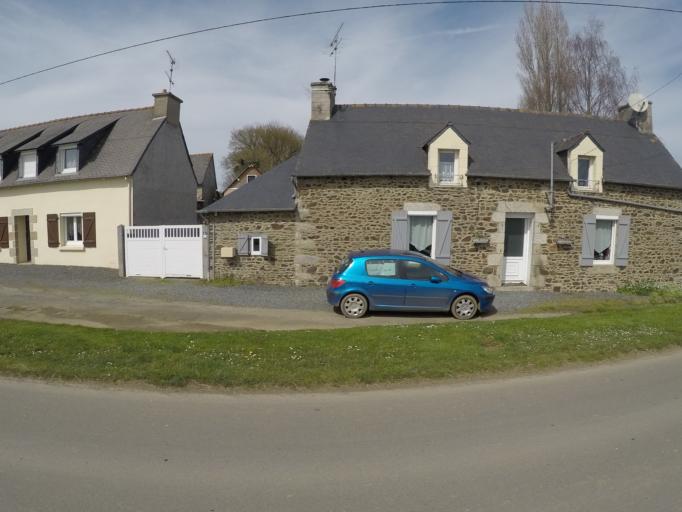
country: FR
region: Brittany
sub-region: Departement des Cotes-d'Armor
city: Plelo
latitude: 48.5755
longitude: -2.9217
